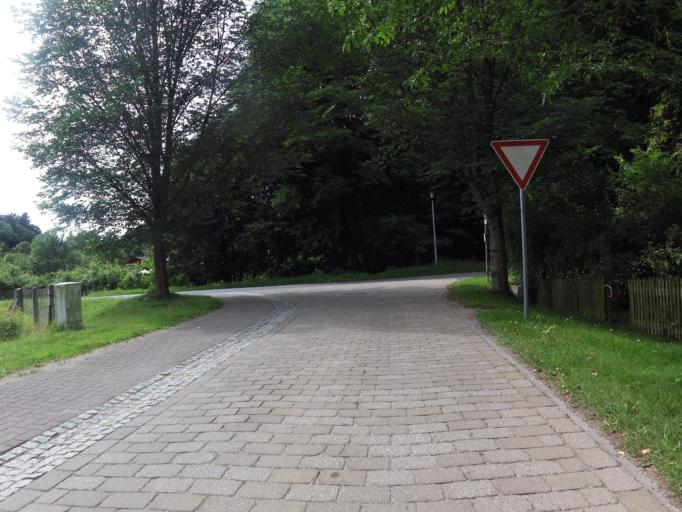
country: DE
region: Mecklenburg-Vorpommern
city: Loitz
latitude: 53.3427
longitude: 13.4267
